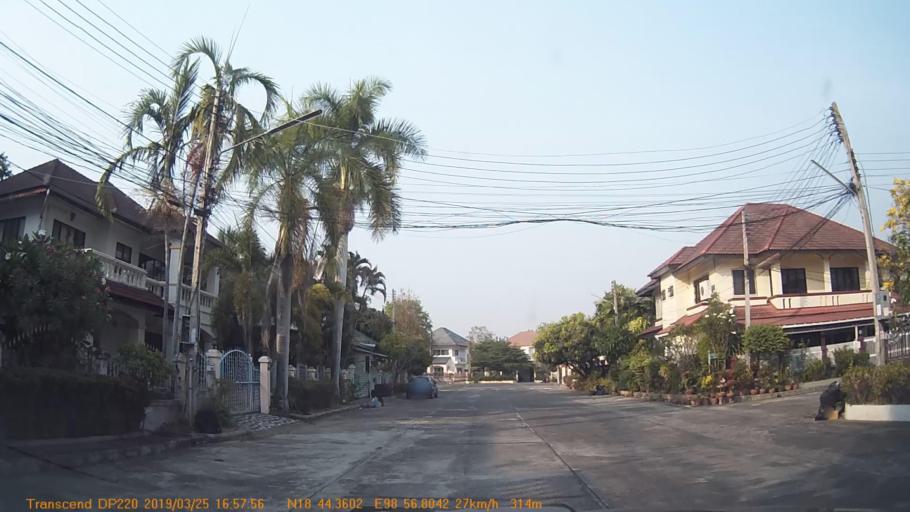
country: TH
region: Chiang Mai
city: Hang Dong
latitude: 18.7393
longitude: 98.9468
